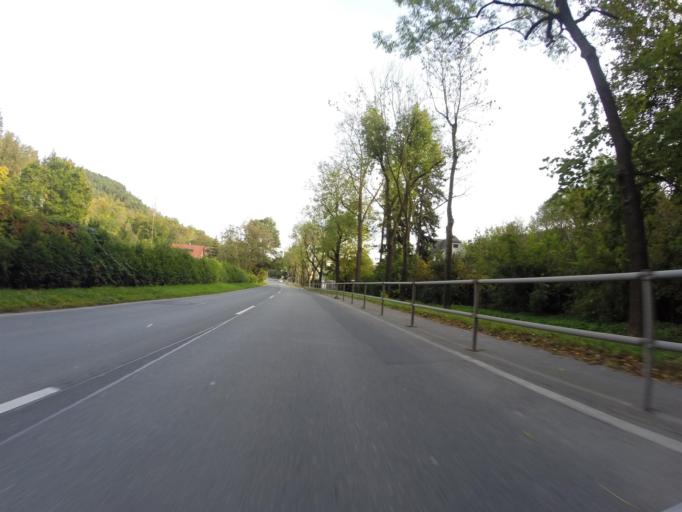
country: DE
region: Thuringia
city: Jena
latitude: 50.9382
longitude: 11.5556
